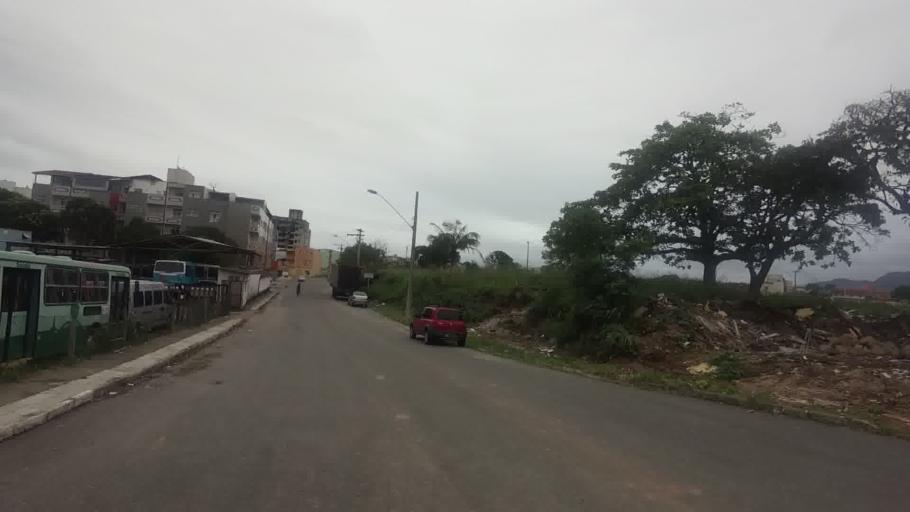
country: BR
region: Espirito Santo
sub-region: Guarapari
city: Guarapari
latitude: -20.6527
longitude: -40.4922
